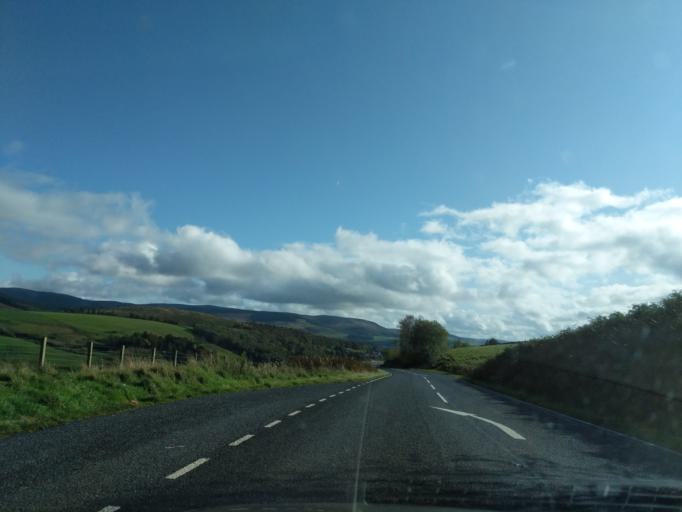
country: GB
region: Scotland
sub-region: Dumfries and Galloway
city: Moffat
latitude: 55.3534
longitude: -3.4674
